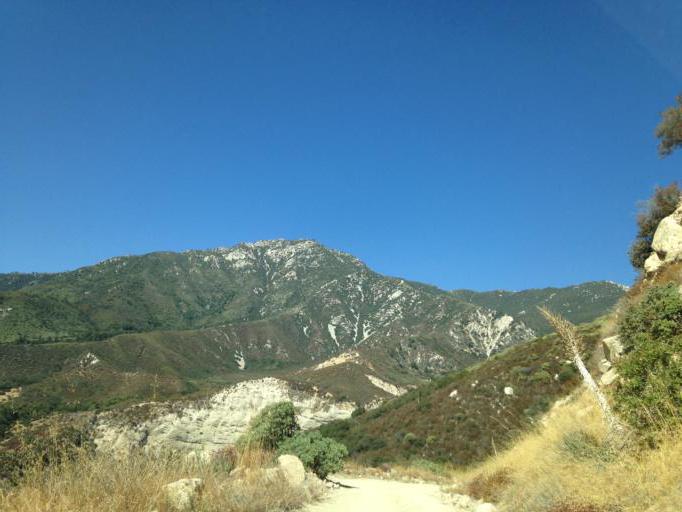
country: US
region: California
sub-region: San Bernardino County
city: Running Springs
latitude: 34.1617
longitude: -117.0466
